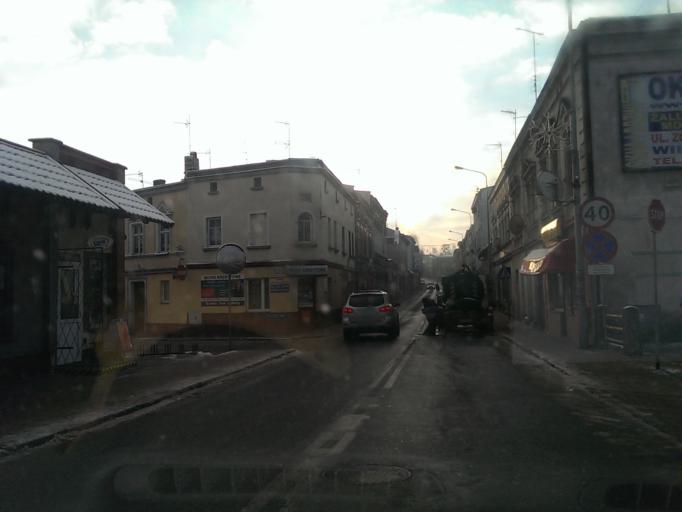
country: PL
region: Kujawsko-Pomorskie
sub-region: Powiat sepolenski
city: Wiecbork
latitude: 53.3501
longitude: 17.4874
